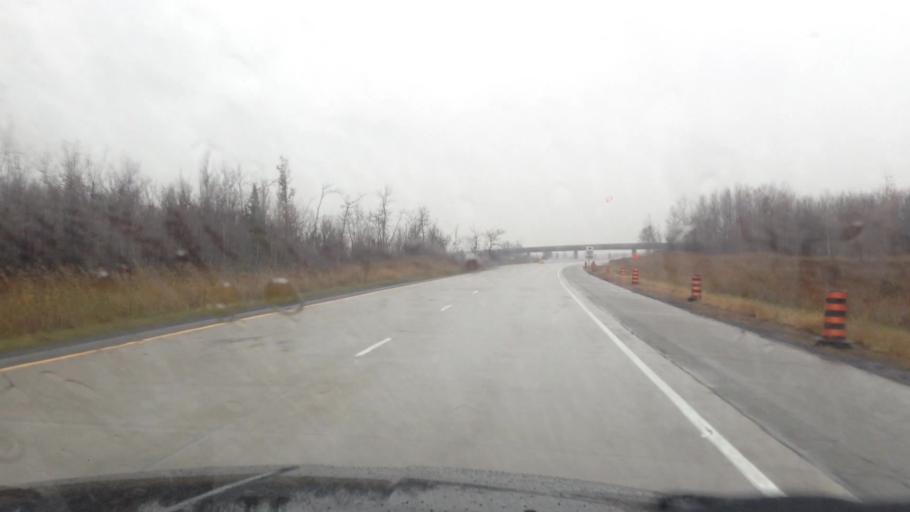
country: CA
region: Ontario
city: Hawkesbury
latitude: 45.4645
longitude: -74.6850
